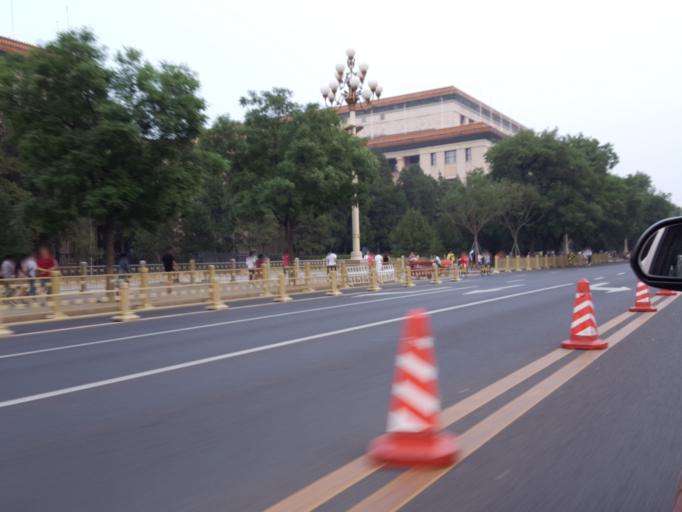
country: CN
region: Beijing
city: Beijing
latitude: 39.9056
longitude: 116.3854
